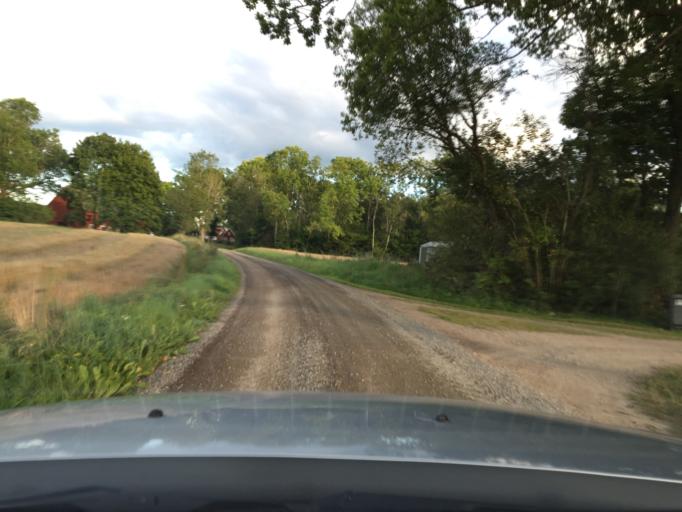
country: SE
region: Skane
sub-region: Hassleholms Kommun
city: Sosdala
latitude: 56.0324
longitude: 13.7146
